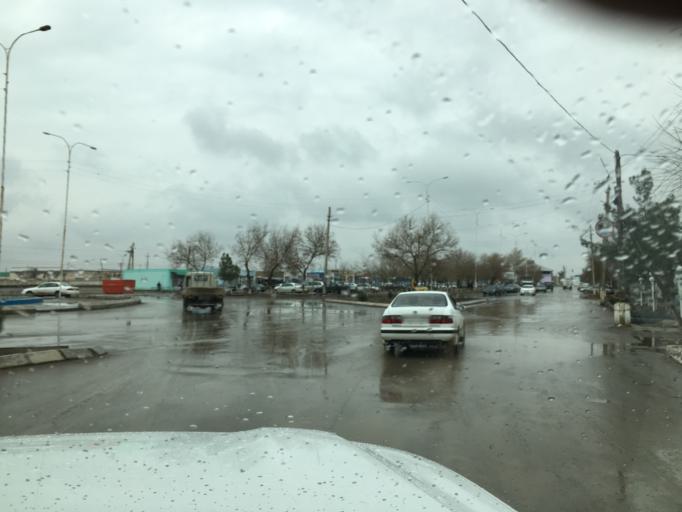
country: TM
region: Mary
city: Yoloeten
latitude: 37.2922
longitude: 62.3575
